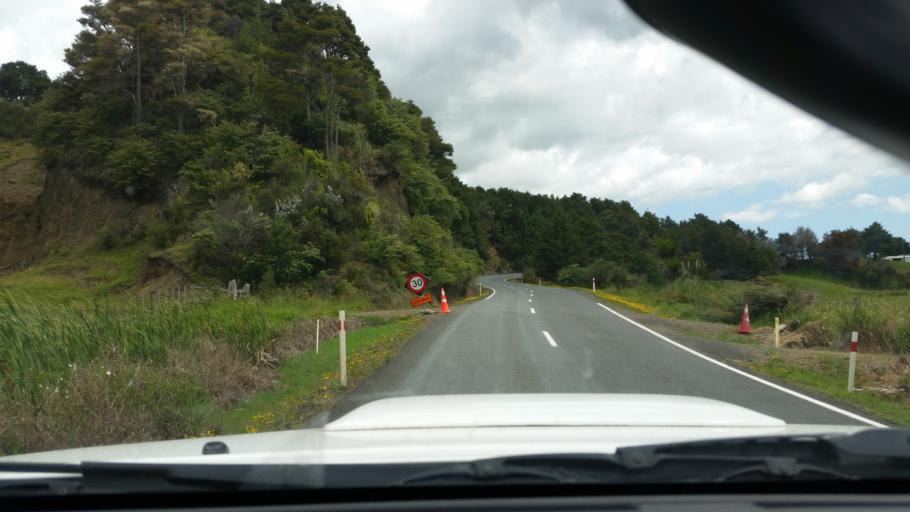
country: NZ
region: Northland
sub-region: Kaipara District
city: Dargaville
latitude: -35.7772
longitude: 173.9073
